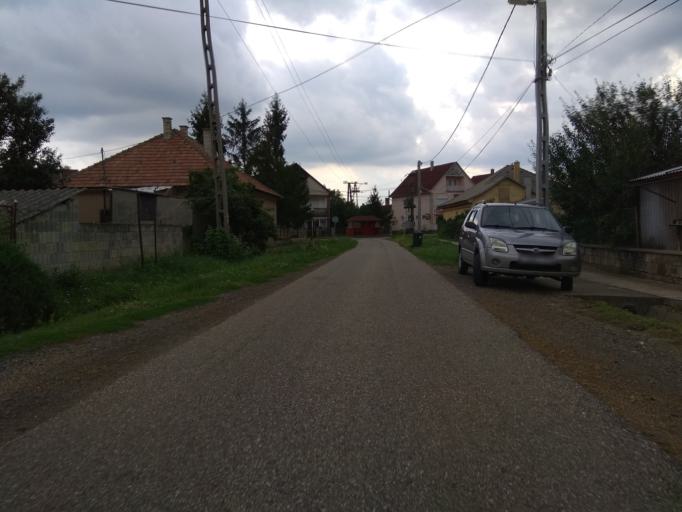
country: HU
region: Borsod-Abauj-Zemplen
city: Bekecs
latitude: 48.1489
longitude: 21.1621
